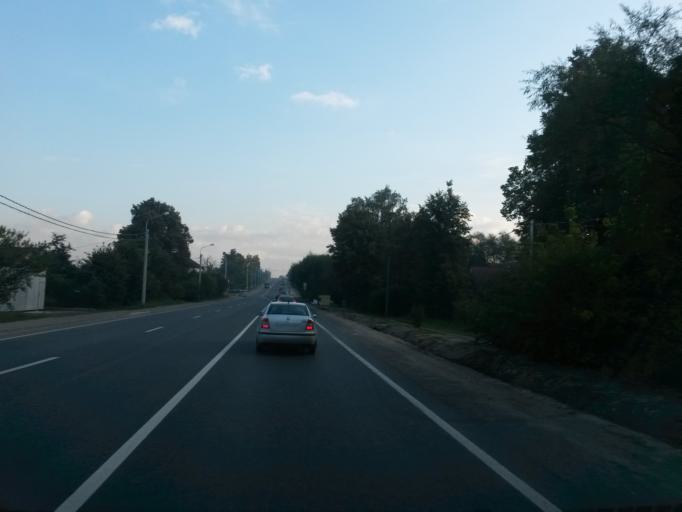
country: RU
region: Moskovskaya
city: Vostryakovo
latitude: 55.3824
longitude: 37.7848
